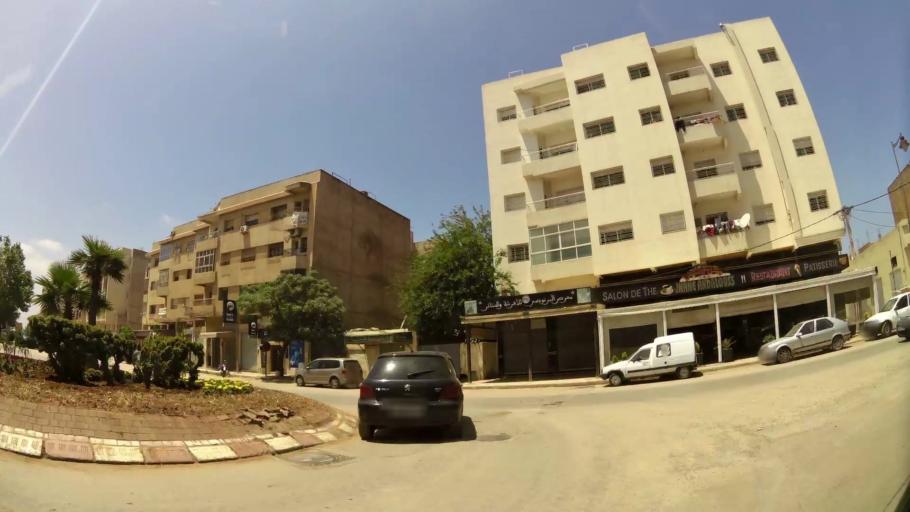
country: MA
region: Fes-Boulemane
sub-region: Fes
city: Fes
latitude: 34.0236
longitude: -5.0368
